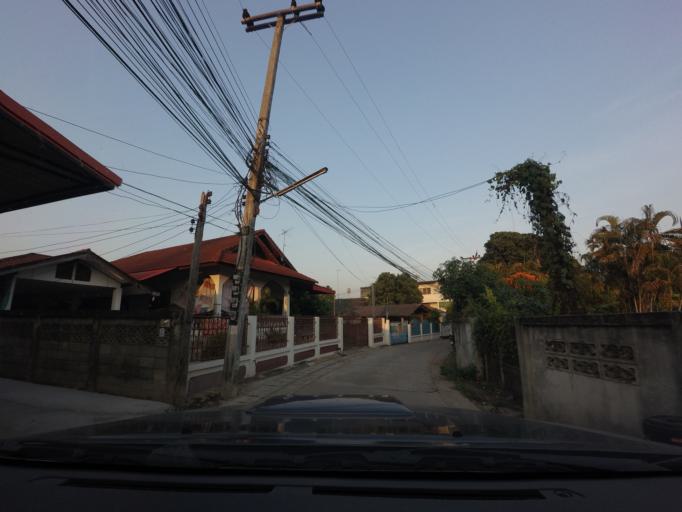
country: TH
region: Chiang Mai
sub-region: Amphoe Chiang Dao
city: Chiang Dao
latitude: 19.3674
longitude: 98.9641
